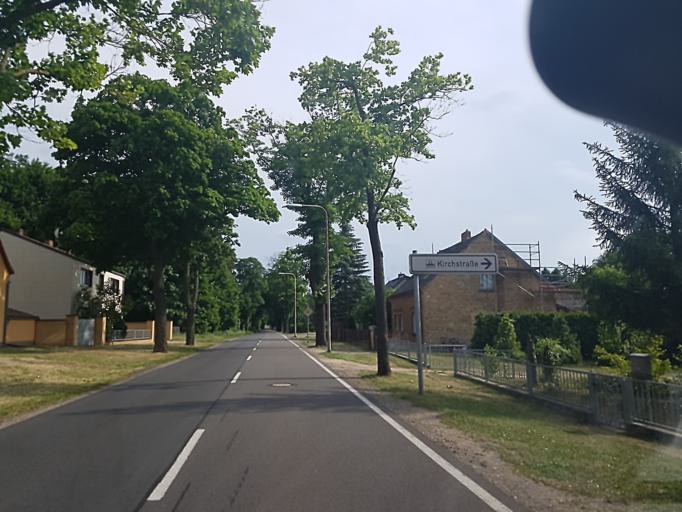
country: DE
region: Saxony-Anhalt
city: Nudersdorf
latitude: 51.9373
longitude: 12.6011
